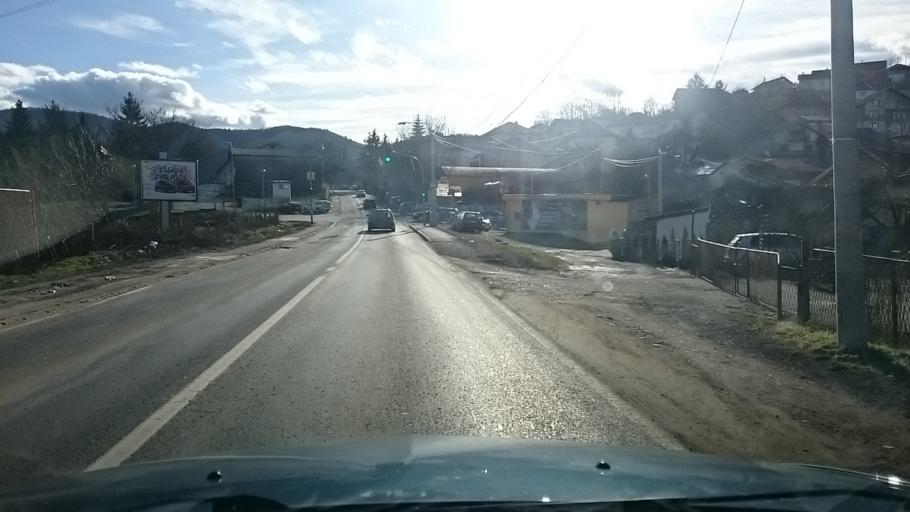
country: BA
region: Republika Srpska
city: Hiseti
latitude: 44.7617
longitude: 17.1749
